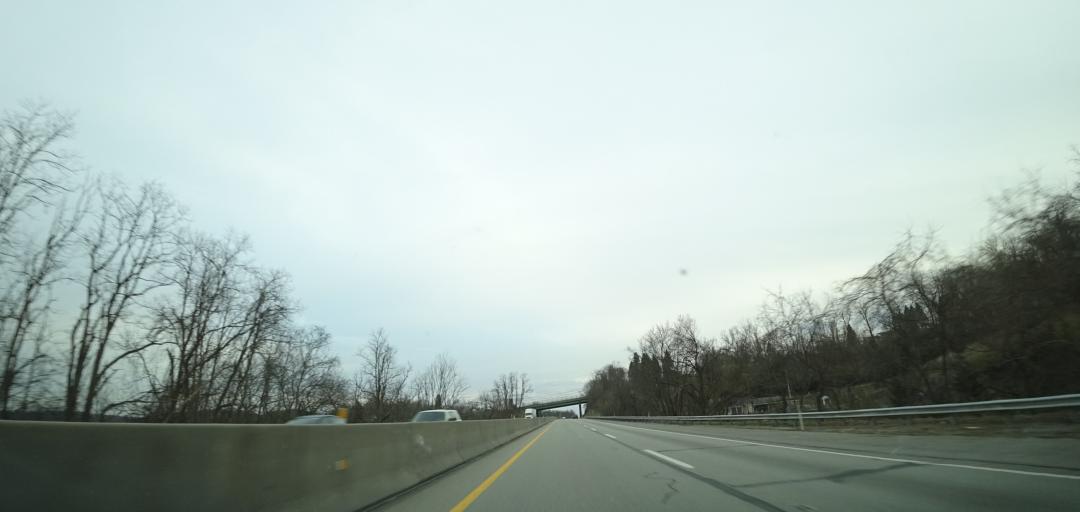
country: US
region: Pennsylvania
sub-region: Allegheny County
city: Plum
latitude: 40.4774
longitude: -79.7682
